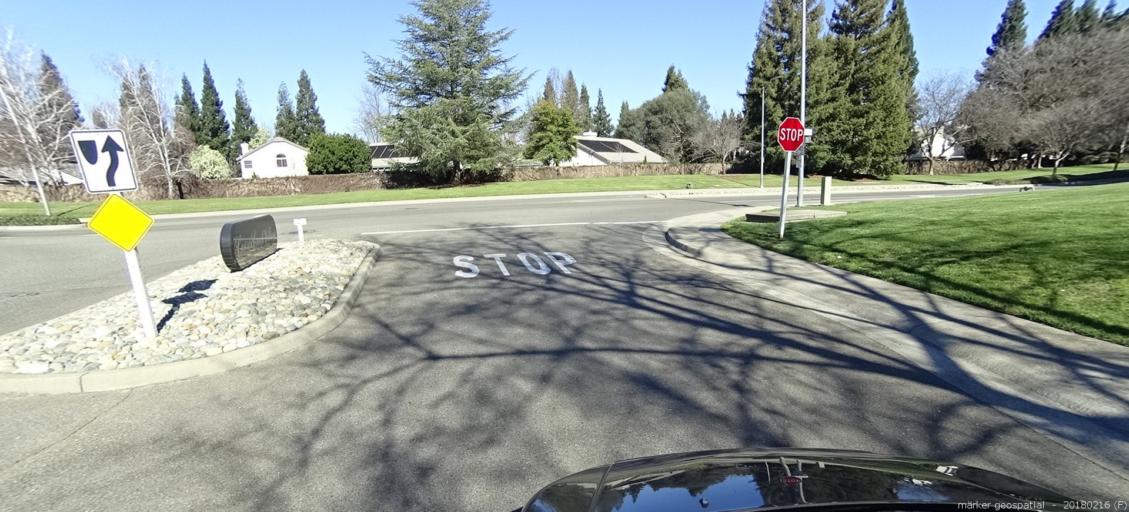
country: US
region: California
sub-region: Sacramento County
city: Gold River
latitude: 38.6254
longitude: -121.2340
